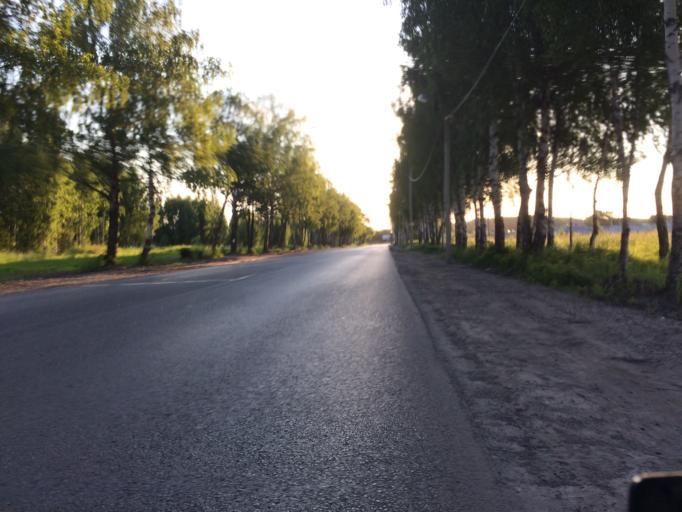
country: RU
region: Mariy-El
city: Medvedevo
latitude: 56.6509
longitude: 47.8338
